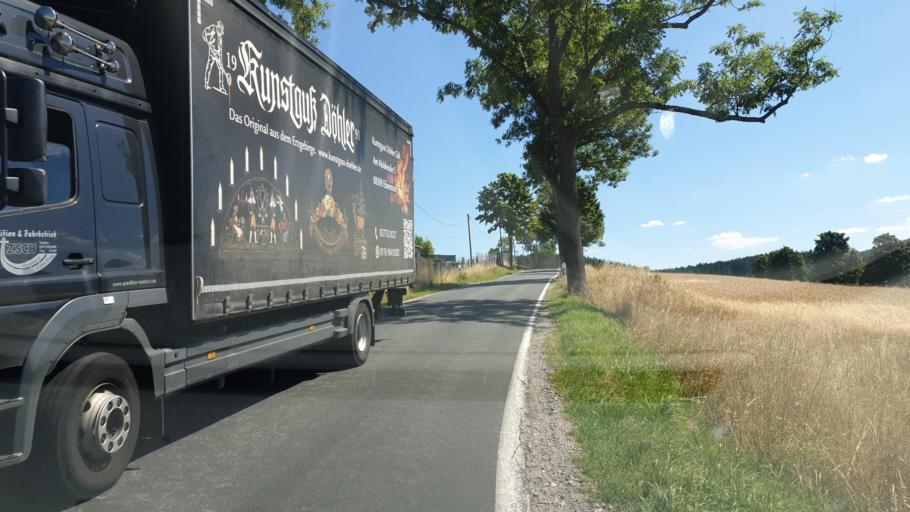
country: DE
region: Saxony
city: Sosa
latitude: 50.5016
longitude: 12.6580
